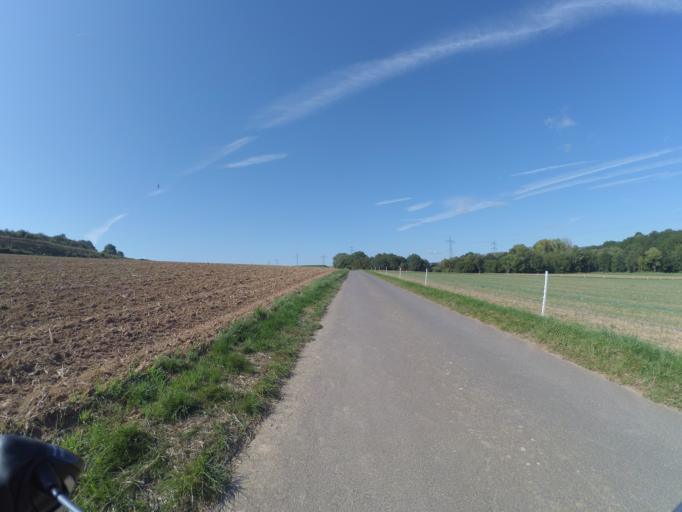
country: DE
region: Rheinland-Pfalz
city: Hetzerath
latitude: 49.8821
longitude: 6.8332
